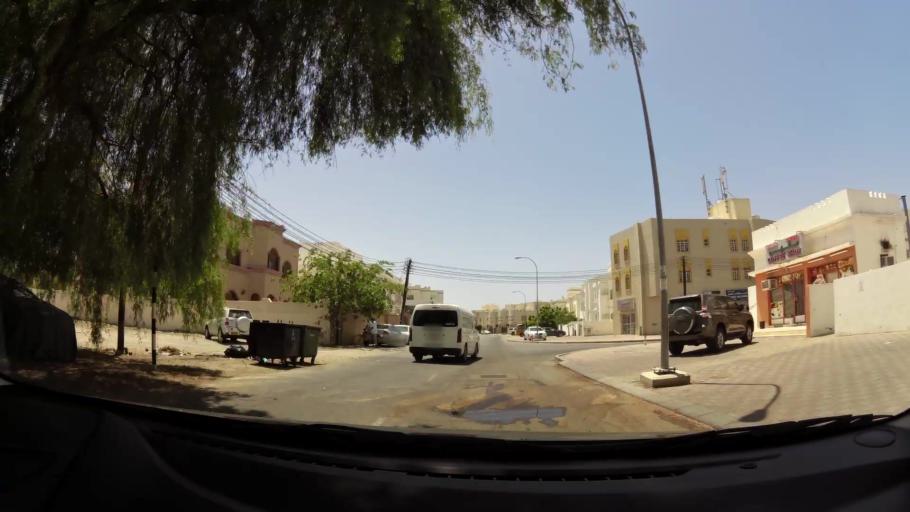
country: OM
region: Muhafazat Masqat
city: Bawshar
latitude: 23.5964
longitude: 58.3820
